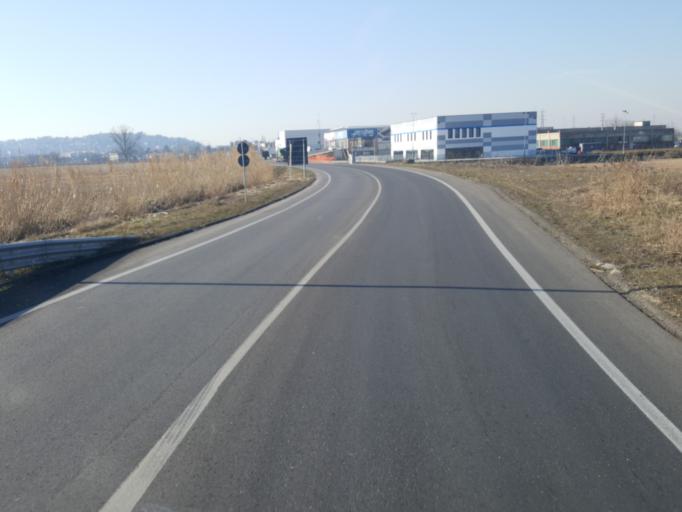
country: IT
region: Piedmont
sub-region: Provincia di Alessandria
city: Tortona
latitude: 44.9177
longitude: 8.8884
